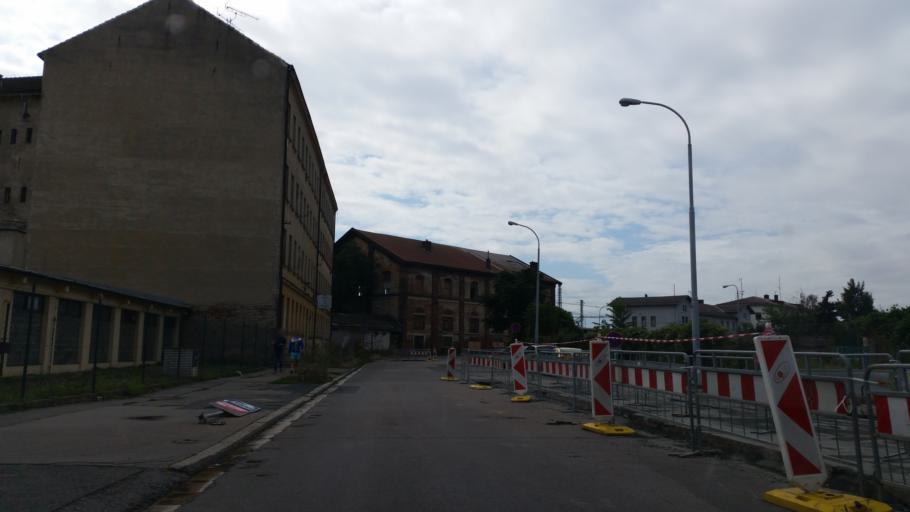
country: CZ
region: South Moravian
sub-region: Mesto Brno
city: Brno
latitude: 49.1850
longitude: 16.6157
